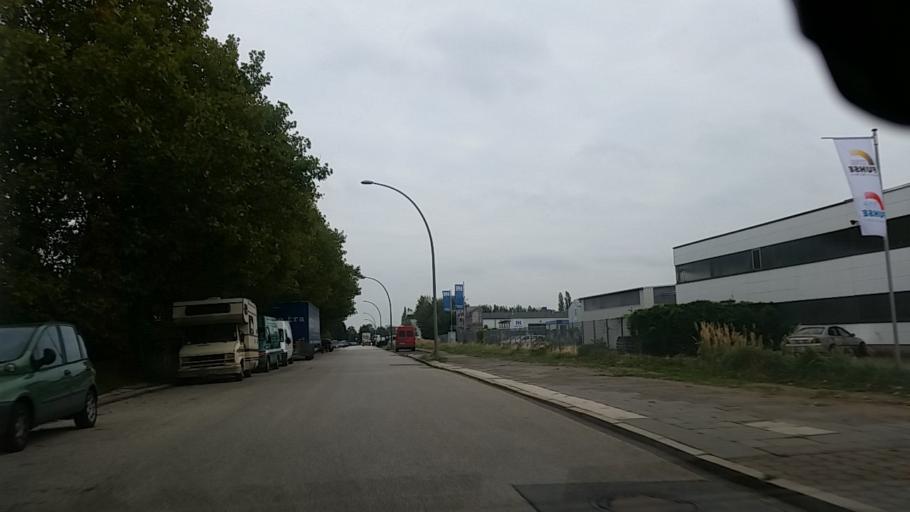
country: DE
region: Hamburg
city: Rothenburgsort
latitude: 53.5224
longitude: 10.0803
